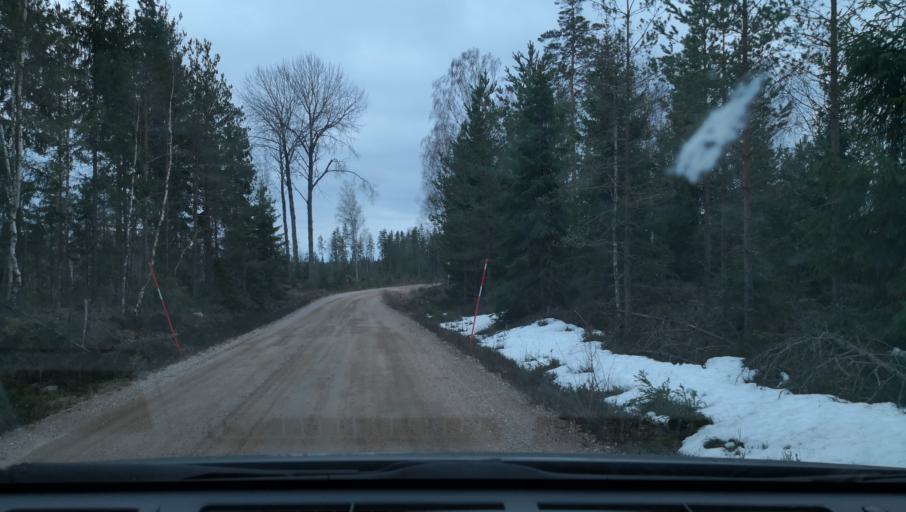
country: SE
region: OErebro
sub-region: Lindesbergs Kommun
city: Fellingsbro
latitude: 59.5897
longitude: 15.5769
